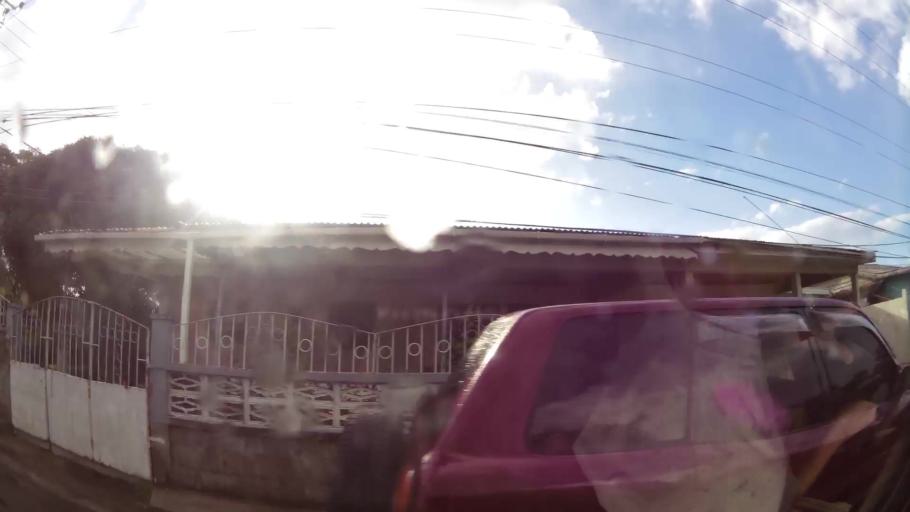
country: DM
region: Saint George
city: Roseau
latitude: 15.3317
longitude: -61.3897
